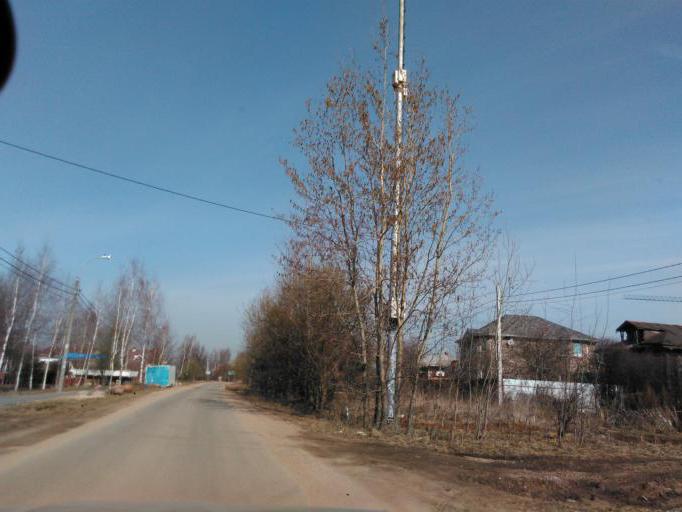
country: RU
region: Moskovskaya
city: Opalikha
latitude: 55.8774
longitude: 37.2677
